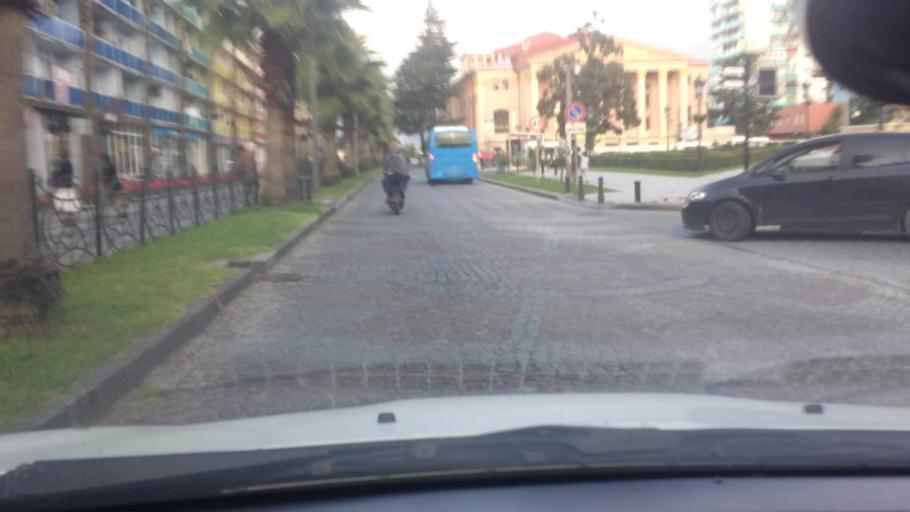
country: GE
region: Ajaria
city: Batumi
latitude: 41.6525
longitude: 41.6365
